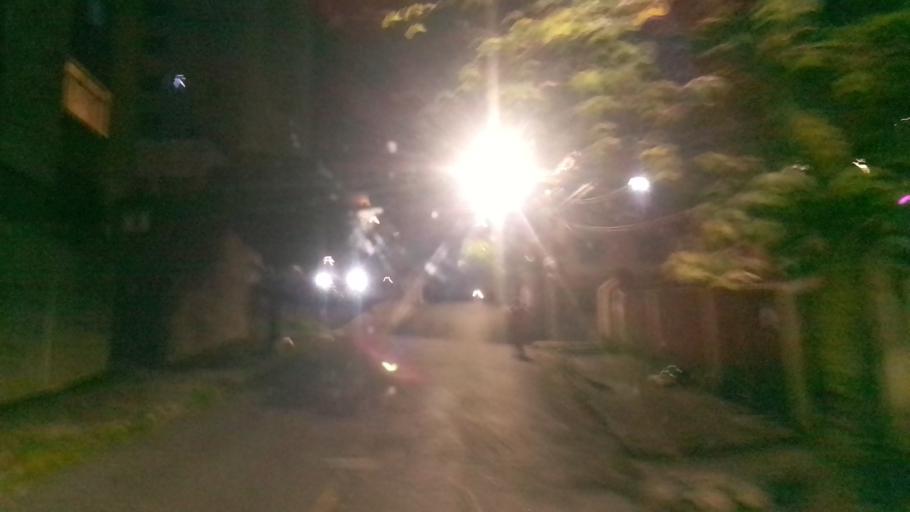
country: BR
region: Minas Gerais
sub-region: Belo Horizonte
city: Belo Horizonte
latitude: -19.9047
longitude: -43.9280
